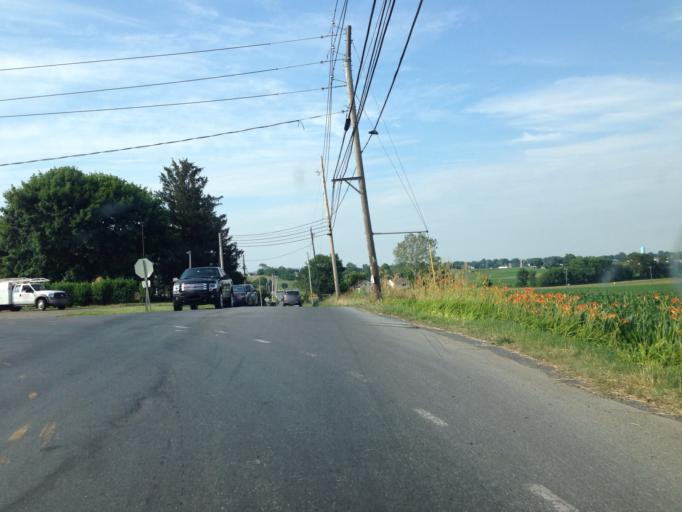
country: US
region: Pennsylvania
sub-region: Lancaster County
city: Brownstown
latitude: 40.0739
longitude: -76.2043
